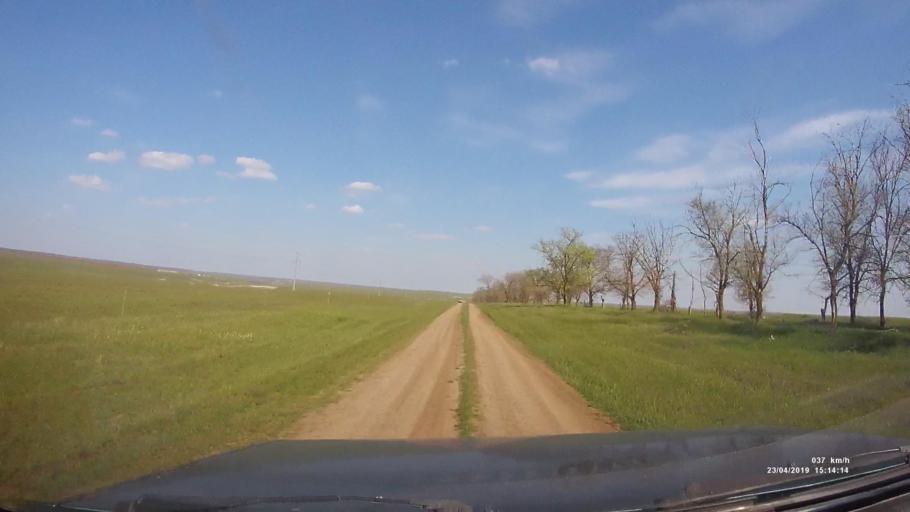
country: RU
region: Rostov
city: Remontnoye
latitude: 46.5397
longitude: 42.9617
